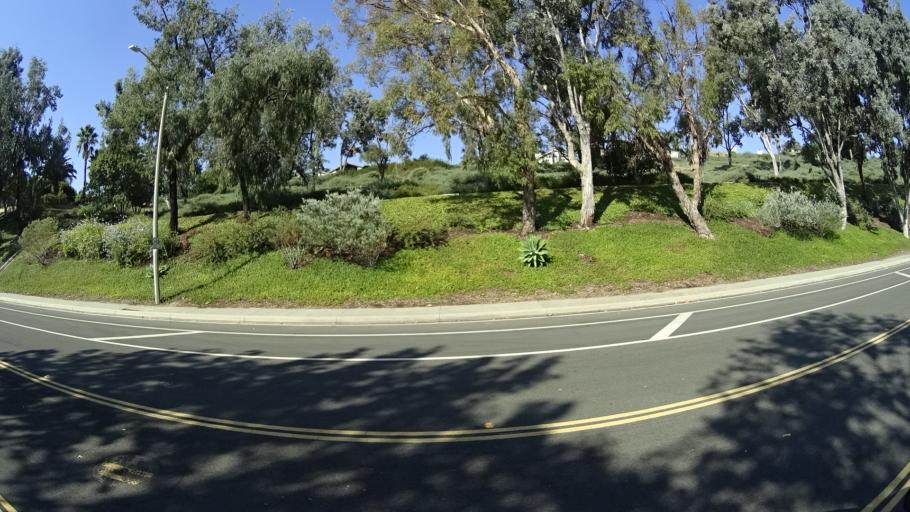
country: US
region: California
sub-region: Orange County
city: San Juan Capistrano
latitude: 33.4752
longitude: -117.6287
